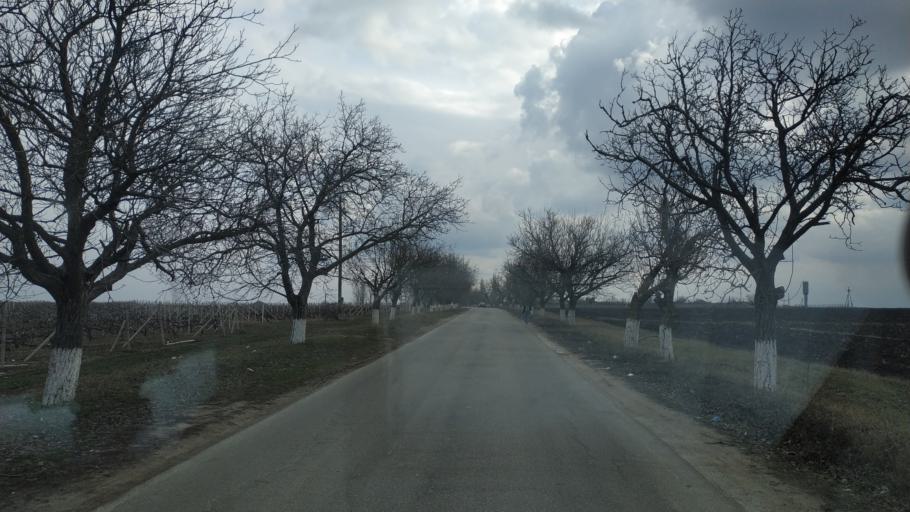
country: MD
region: Anenii Noi
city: Anenii Noi
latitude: 46.8552
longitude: 29.3489
